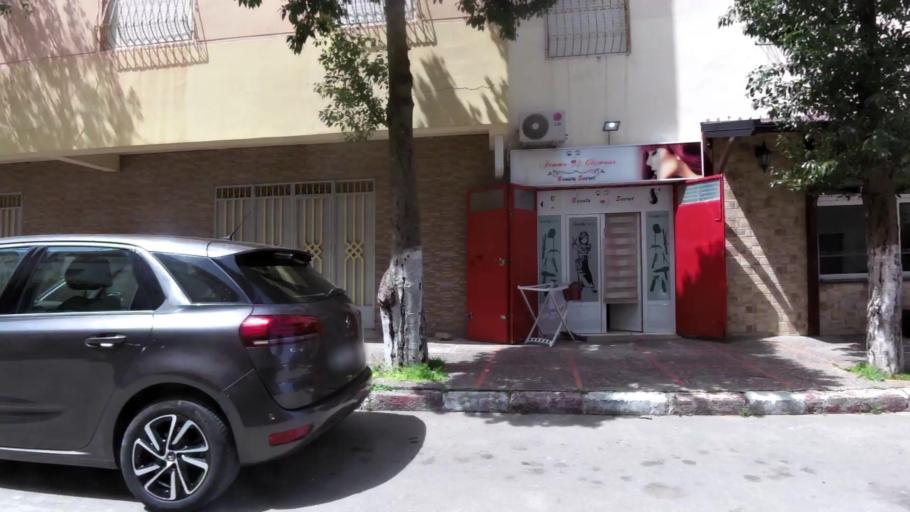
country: MA
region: Tanger-Tetouan
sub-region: Tanger-Assilah
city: Tangier
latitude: 35.7450
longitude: -5.8471
